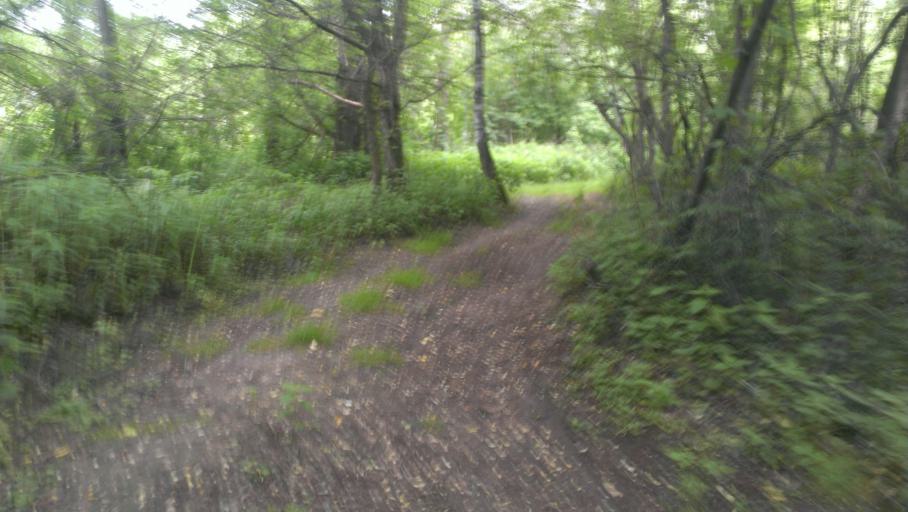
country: RU
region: Altai Krai
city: Sannikovo
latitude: 53.3422
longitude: 84.0590
